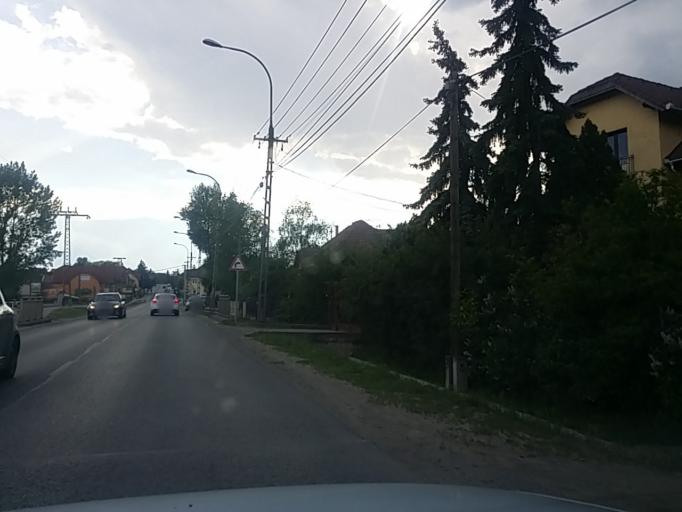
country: HU
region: Pest
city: Veresegyhaz
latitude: 47.6542
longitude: 19.2802
